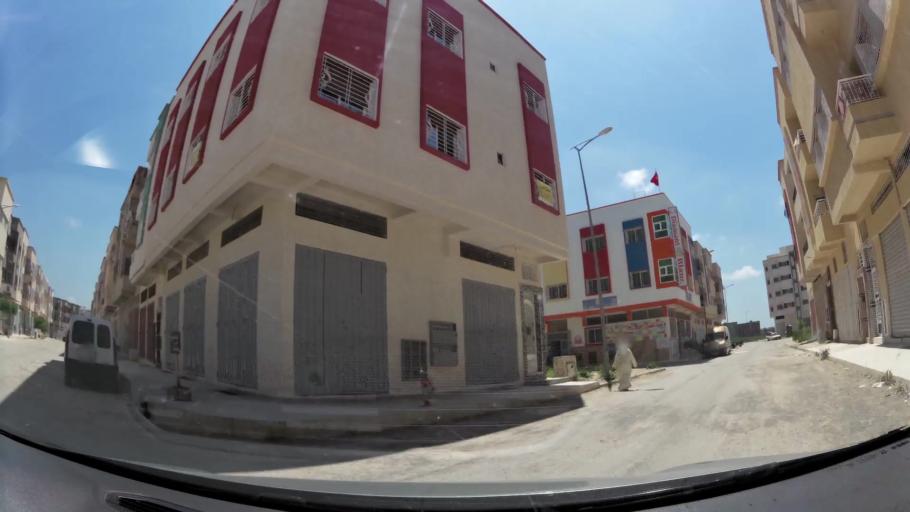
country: MA
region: Fes-Boulemane
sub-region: Fes
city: Fes
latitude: 34.0215
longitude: -5.0578
